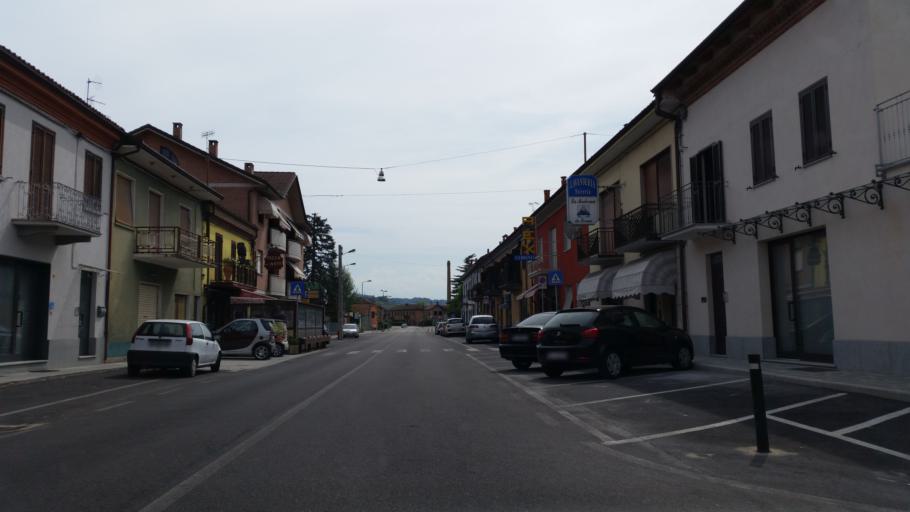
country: IT
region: Piedmont
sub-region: Provincia di Cuneo
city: Grinzane Cavour
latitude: 44.6548
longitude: 7.9800
